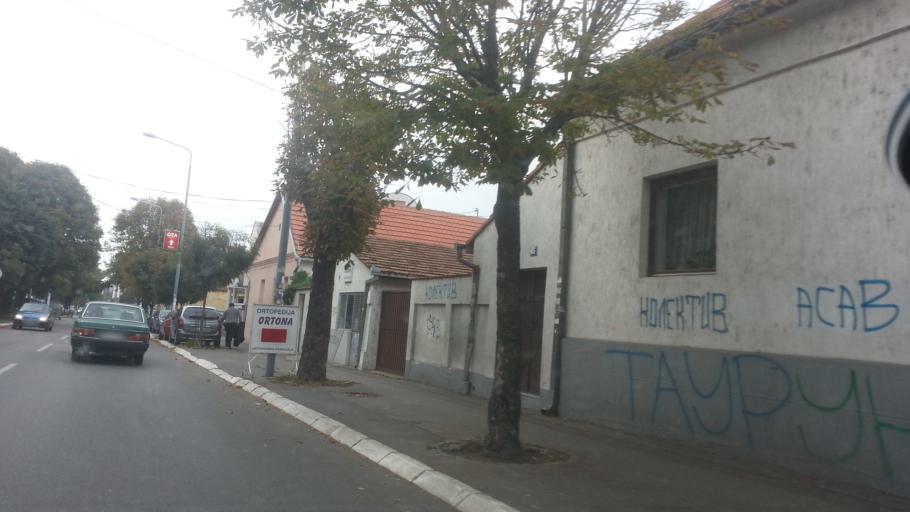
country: RS
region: Central Serbia
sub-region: Belgrade
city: Zemun
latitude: 44.8473
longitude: 20.3965
